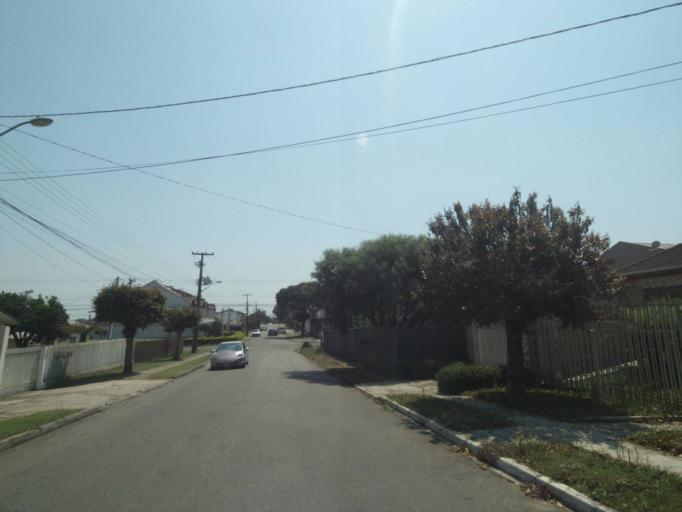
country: BR
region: Parana
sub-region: Sao Jose Dos Pinhais
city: Sao Jose dos Pinhais
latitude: -25.5125
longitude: -49.2653
